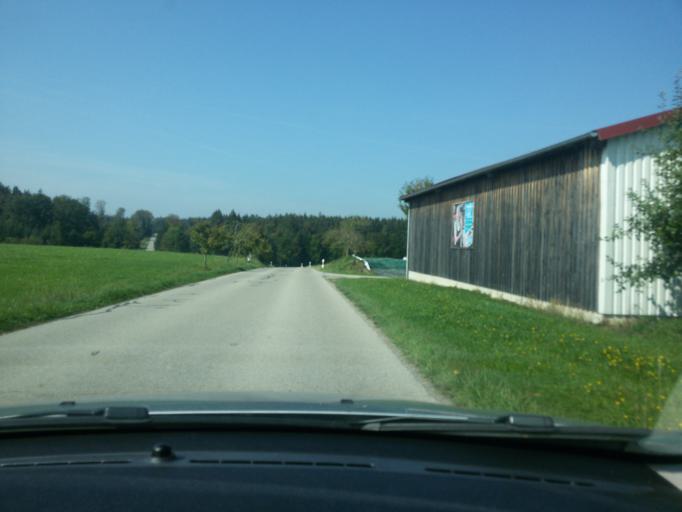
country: DE
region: Bavaria
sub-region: Swabia
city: Hiltenfingen
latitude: 48.1848
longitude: 10.6778
